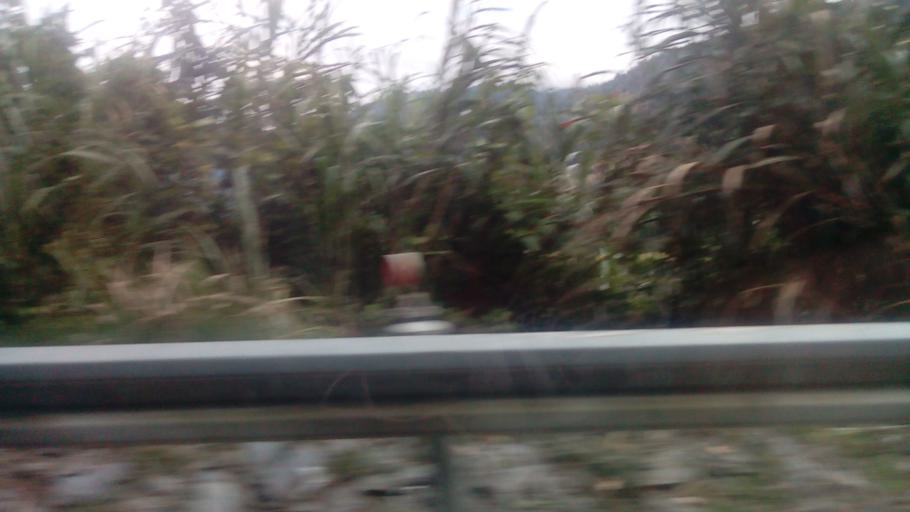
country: TW
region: Taiwan
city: Daxi
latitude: 24.4509
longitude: 121.3898
